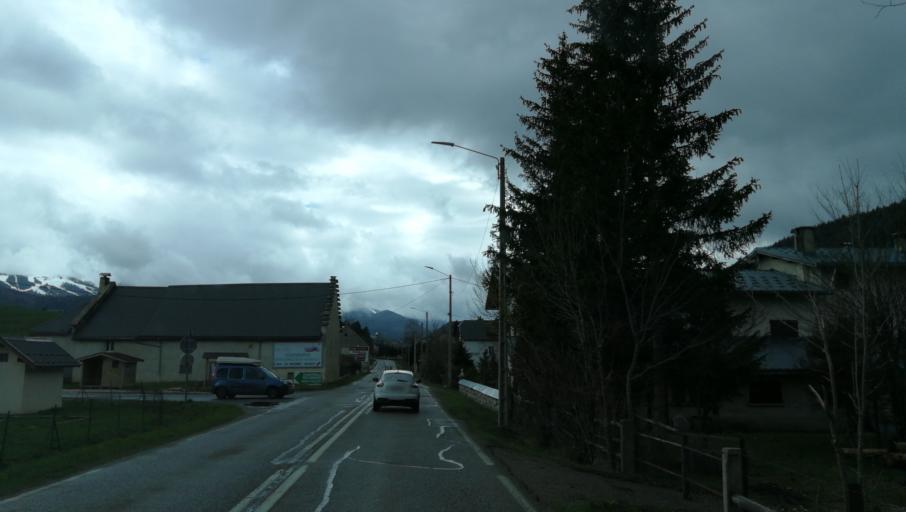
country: FR
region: Rhone-Alpes
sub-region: Departement de l'Isere
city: Villard-de-Lans
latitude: 45.0868
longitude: 5.5546
